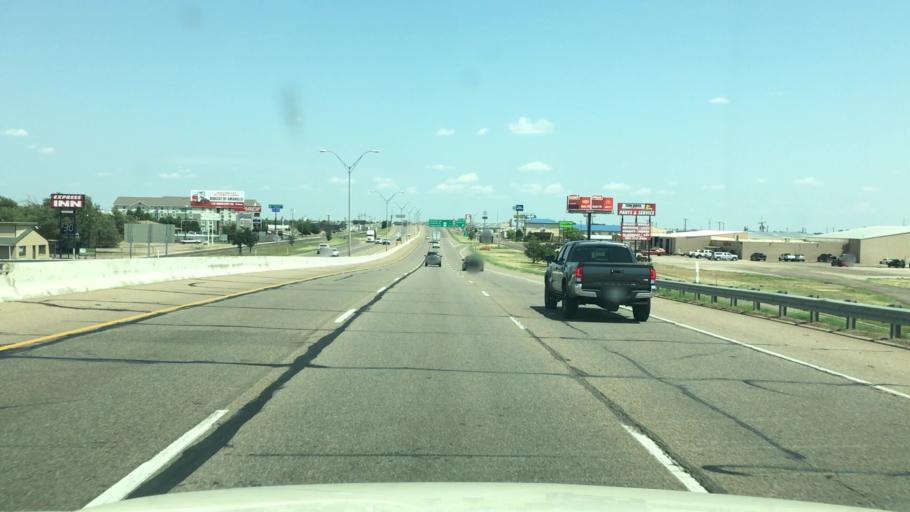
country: US
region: Texas
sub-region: Potter County
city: Amarillo
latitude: 35.1925
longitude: -101.7861
